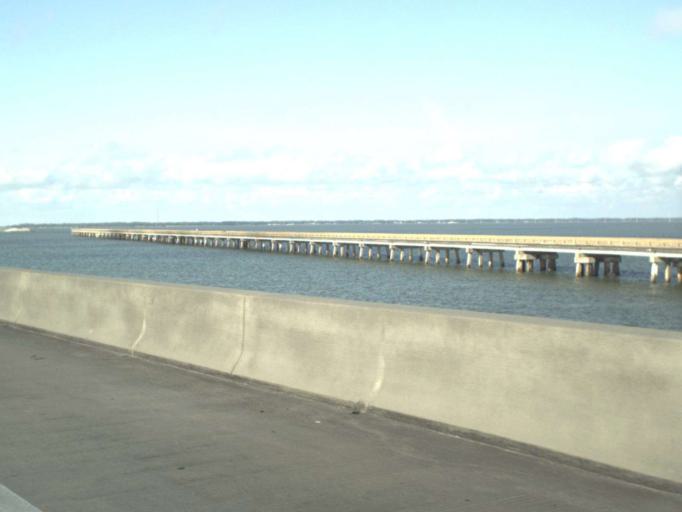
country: US
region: Florida
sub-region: Franklin County
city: Eastpoint
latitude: 29.6739
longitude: -84.8701
